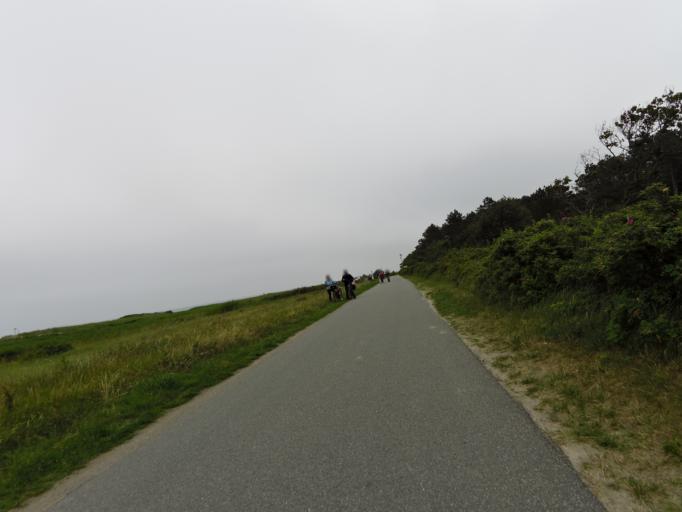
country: DE
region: Lower Saxony
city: Nordholz
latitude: 53.8643
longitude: 8.5973
